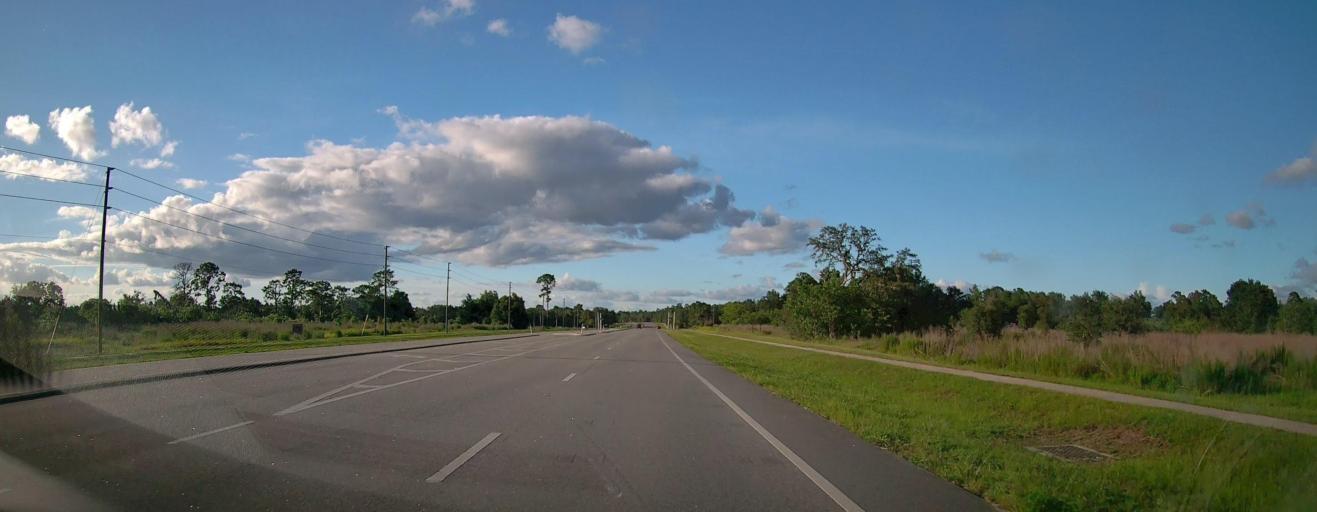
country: US
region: Florida
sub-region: Marion County
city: Belleview
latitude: 29.0512
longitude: -82.0173
